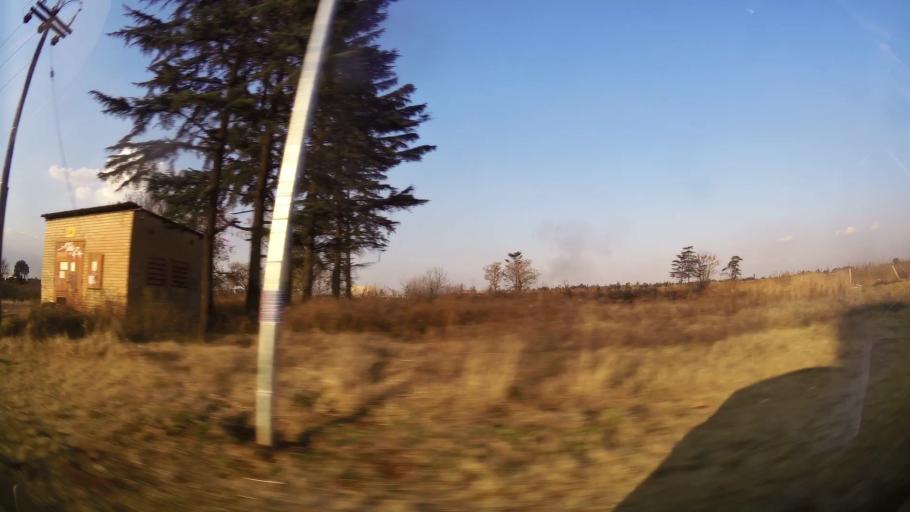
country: ZA
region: Gauteng
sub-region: Ekurhuleni Metropolitan Municipality
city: Germiston
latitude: -26.2976
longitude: 28.2313
